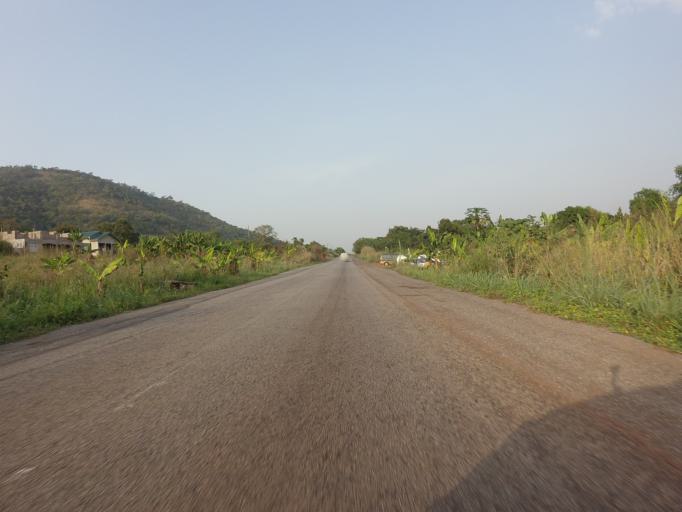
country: GH
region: Volta
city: Ho
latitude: 6.5594
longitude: 0.2967
